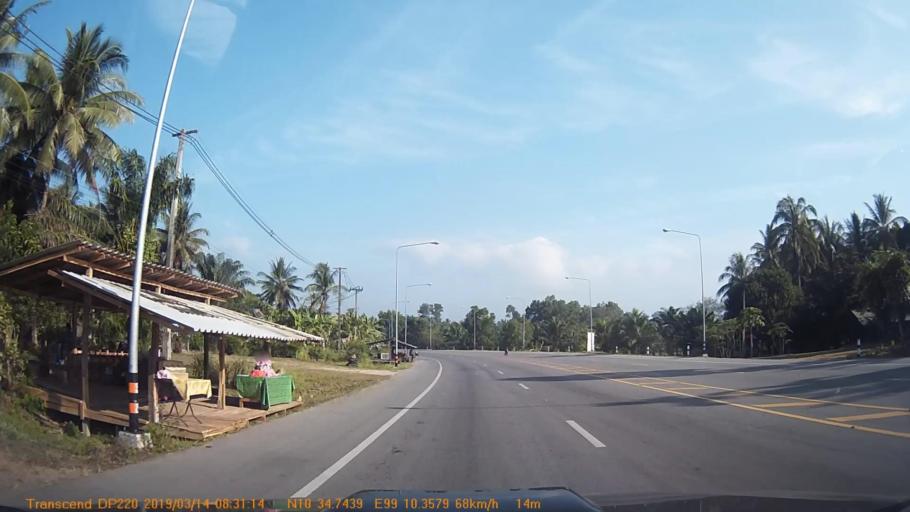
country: TH
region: Chumphon
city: Chumphon
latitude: 10.5790
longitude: 99.1726
